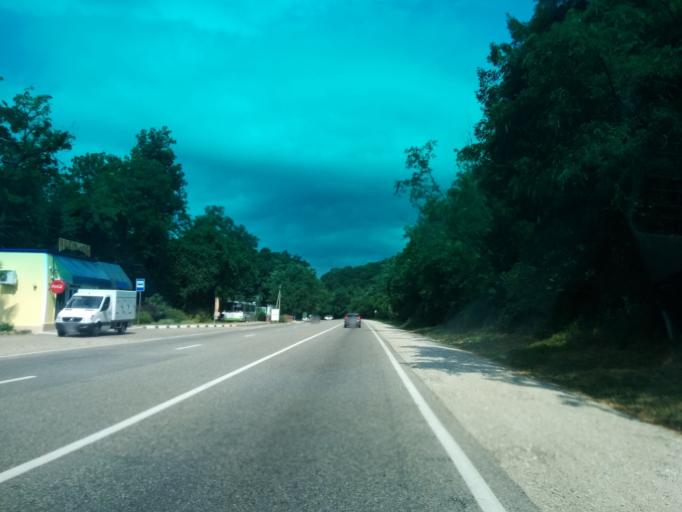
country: RU
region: Krasnodarskiy
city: Nebug
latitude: 44.1687
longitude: 38.9865
